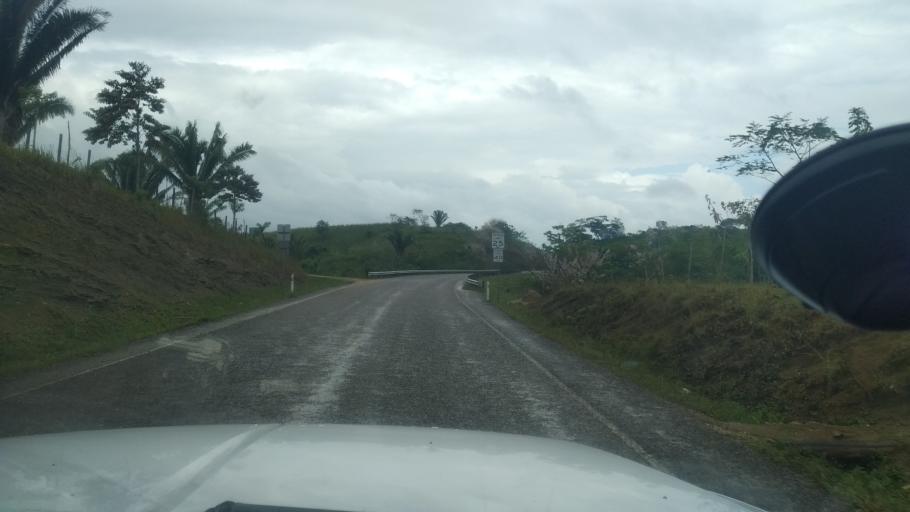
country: GT
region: Peten
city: San Luis
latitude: 16.1847
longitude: -89.1971
